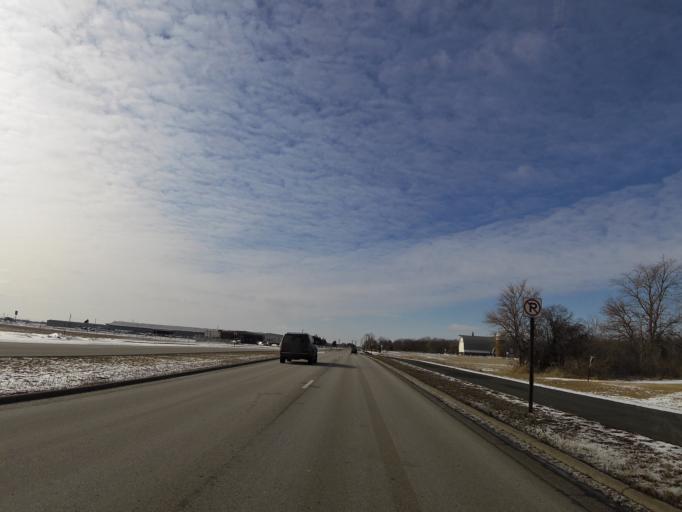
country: US
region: Minnesota
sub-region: Hennepin County
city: Eden Prairie
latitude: 44.8304
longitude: -93.4522
